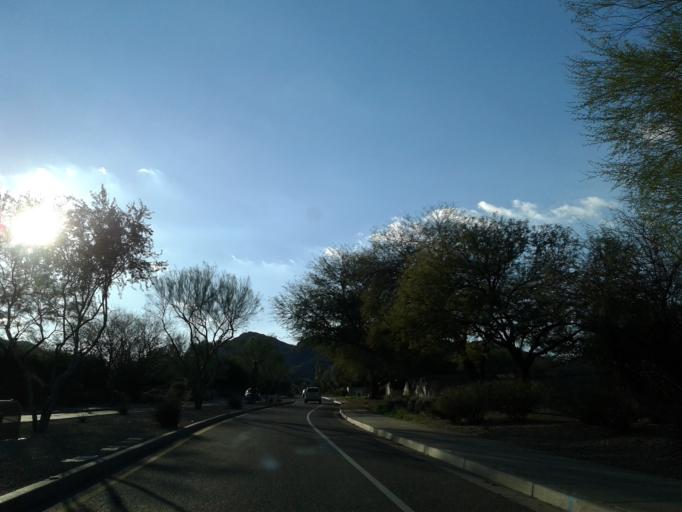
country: US
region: Arizona
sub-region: Maricopa County
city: Paradise Valley
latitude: 33.5682
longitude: -111.9700
